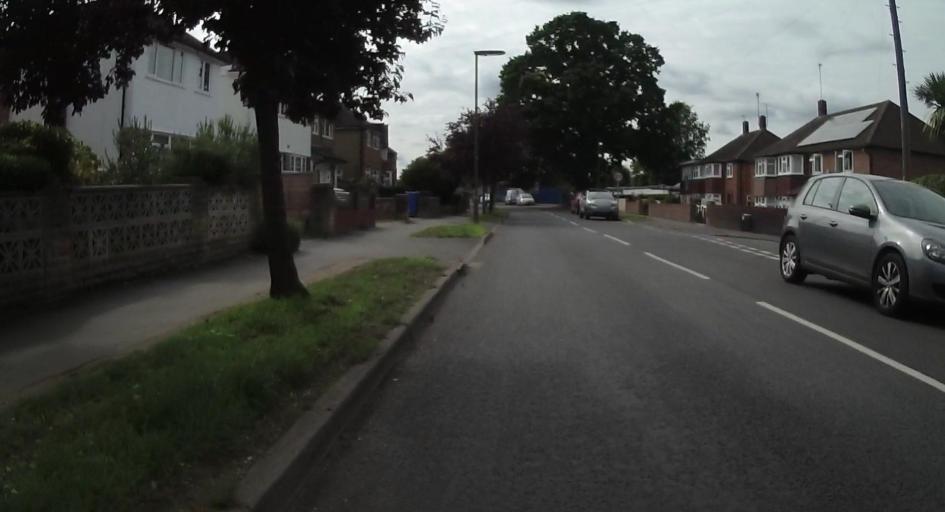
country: GB
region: England
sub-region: Surrey
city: Woking
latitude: 51.3257
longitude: -0.5739
